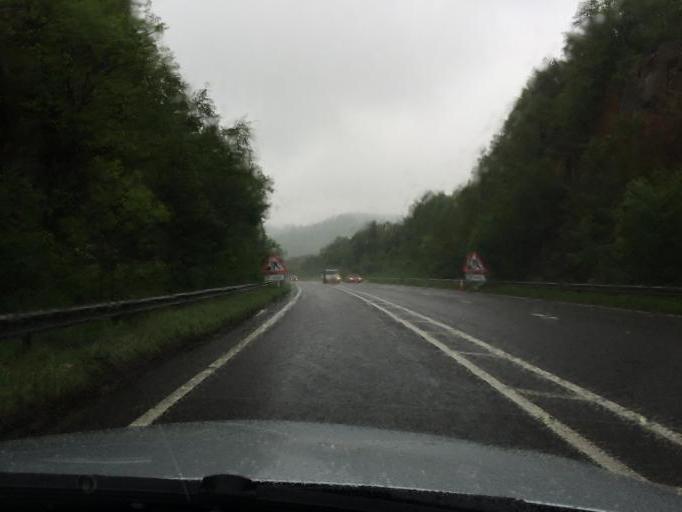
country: GB
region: England
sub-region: Barnsley
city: Wortley
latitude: 53.4859
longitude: -1.5493
